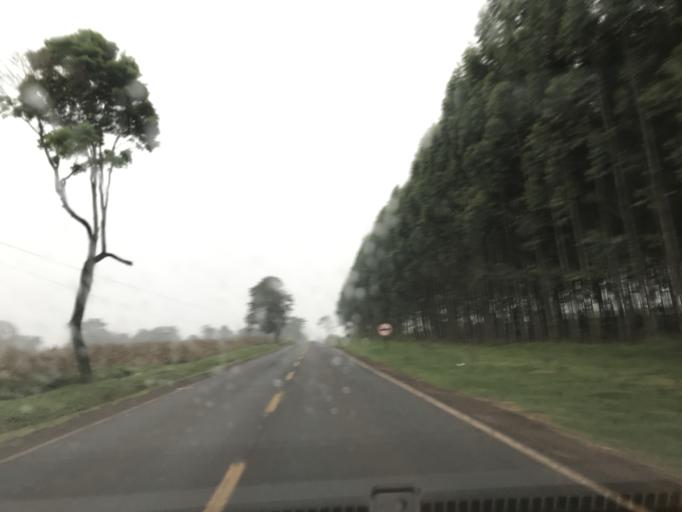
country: PY
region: Canindeyu
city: Salto del Guaira
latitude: -24.1128
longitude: -54.1122
